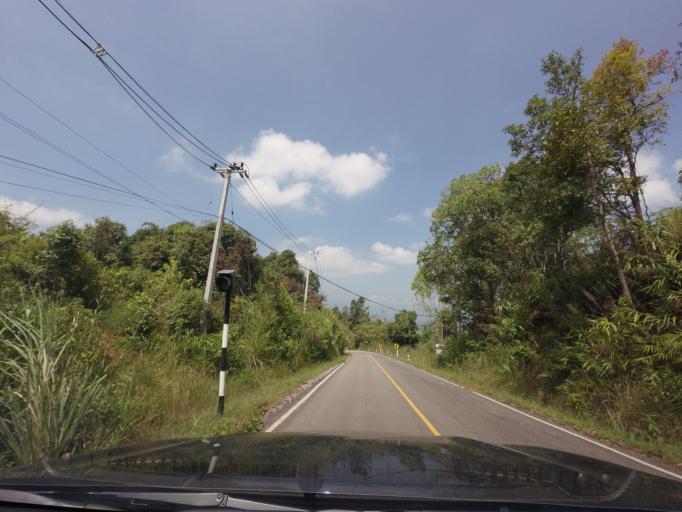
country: TH
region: Loei
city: Na Haeo
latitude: 17.4871
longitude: 100.9039
